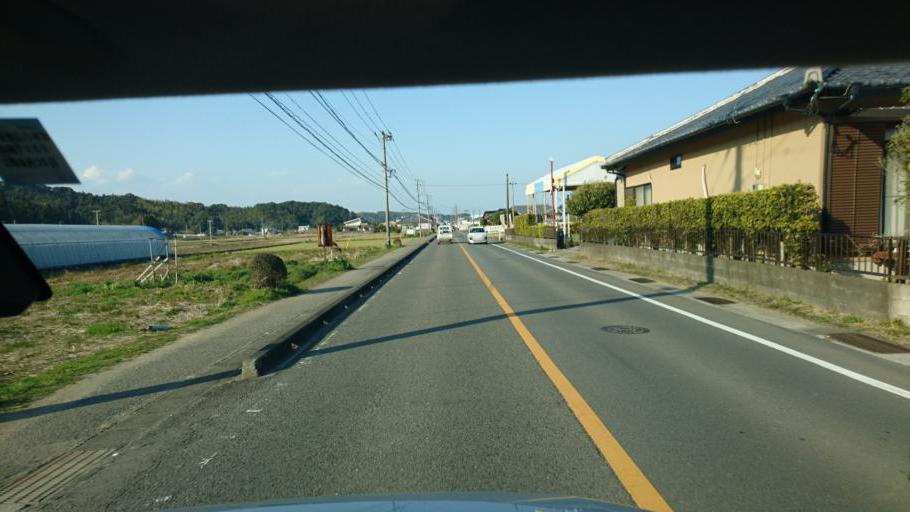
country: JP
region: Miyazaki
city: Miyazaki-shi
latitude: 31.9909
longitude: 131.4395
